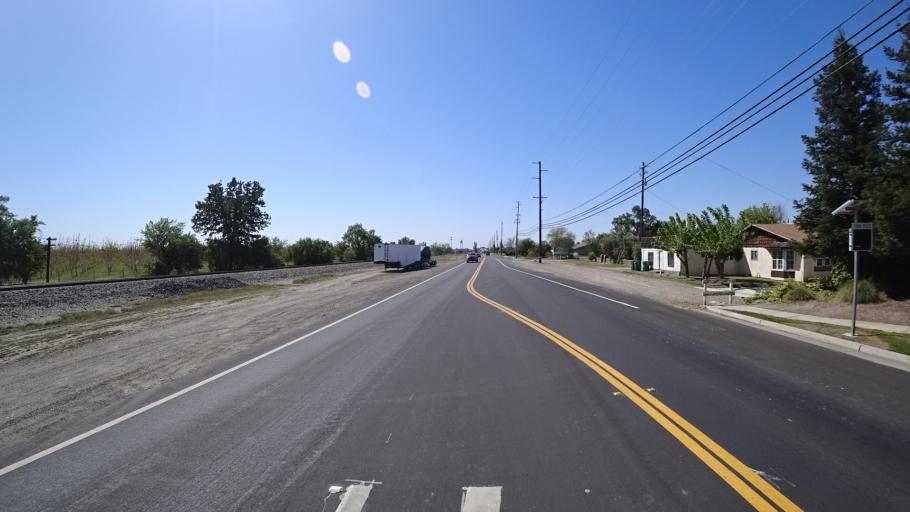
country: US
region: California
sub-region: Glenn County
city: Orland
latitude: 39.7582
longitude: -122.1970
